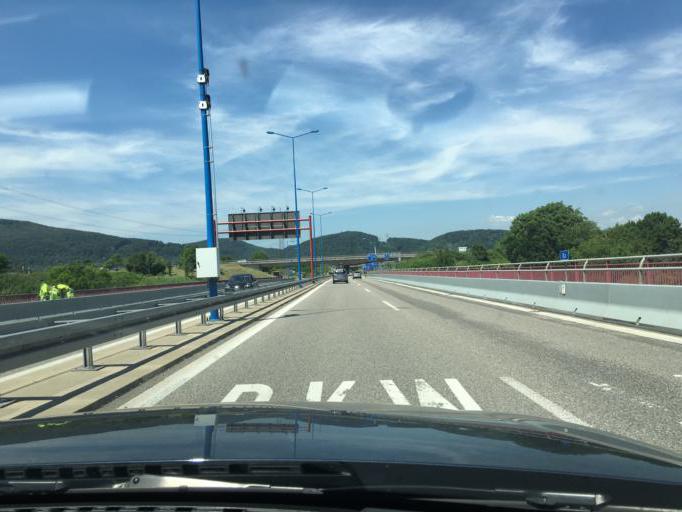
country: DE
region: Baden-Wuerttemberg
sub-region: Freiburg Region
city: Rheinfelden (Baden)
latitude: 47.5483
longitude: 7.7584
